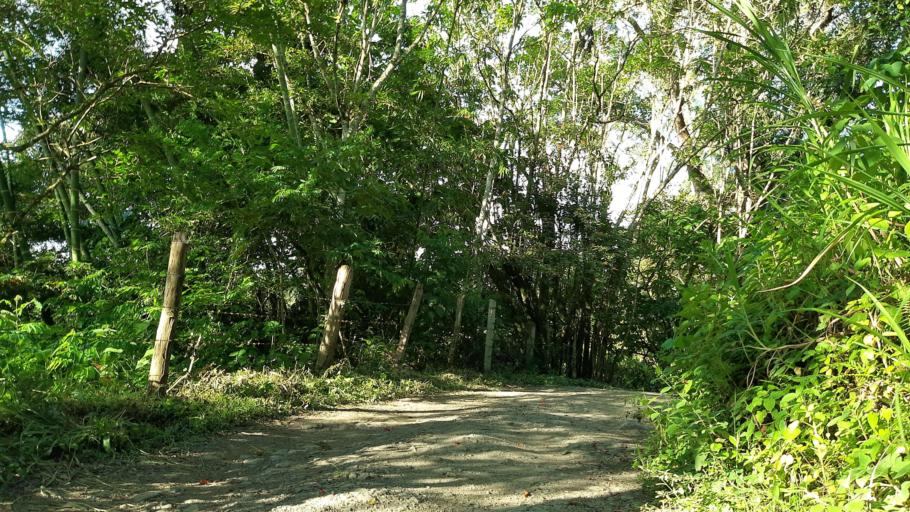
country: CO
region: Boyaca
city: Garagoa
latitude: 5.0720
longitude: -73.3777
